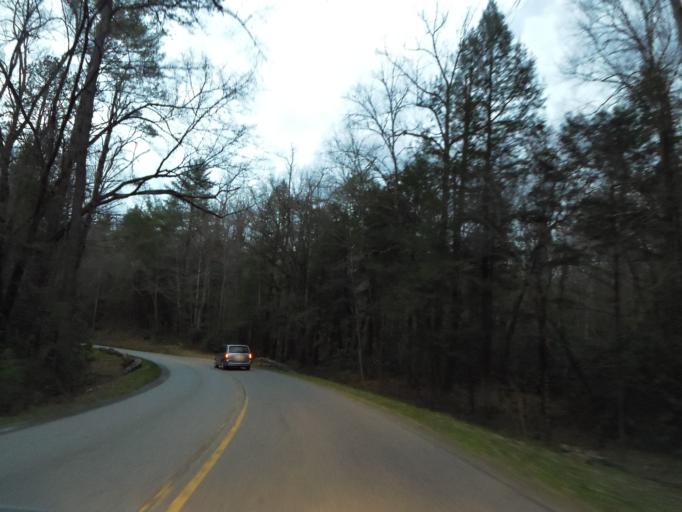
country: US
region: Tennessee
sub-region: Blount County
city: Wildwood
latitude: 35.6164
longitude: -83.7383
